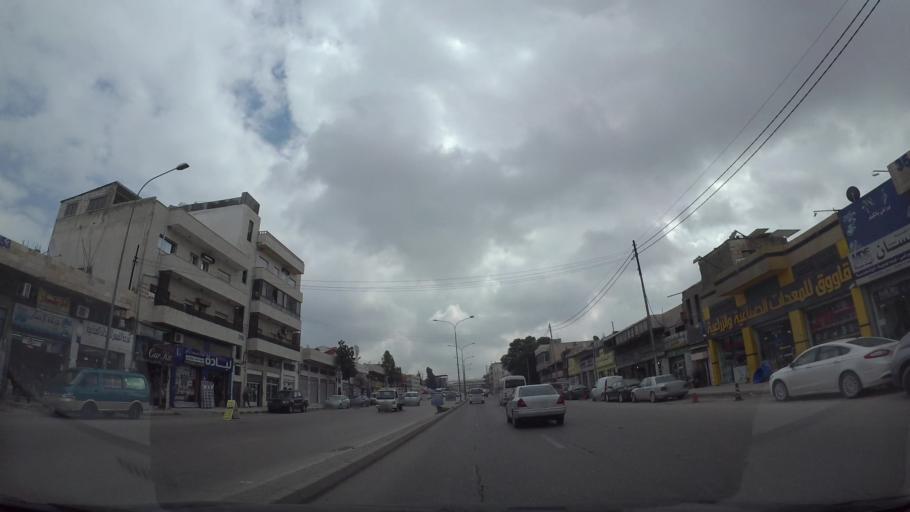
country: JO
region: Amman
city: Al Quwaysimah
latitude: 31.9169
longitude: 35.9385
